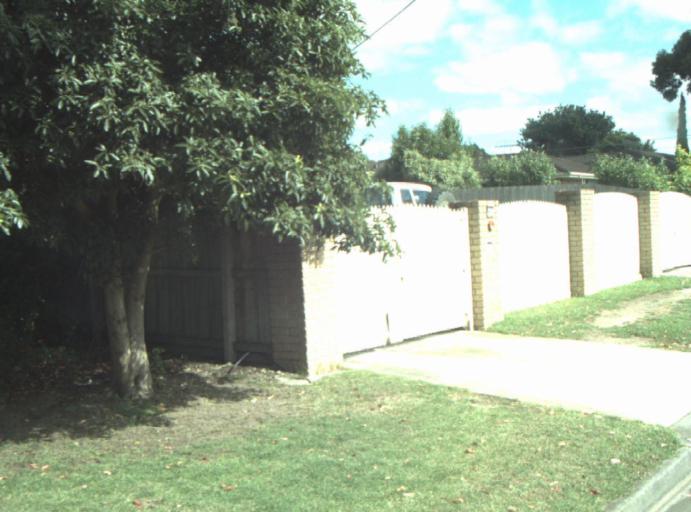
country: AU
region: Victoria
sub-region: Greater Geelong
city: Breakwater
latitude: -38.2103
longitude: 144.3362
